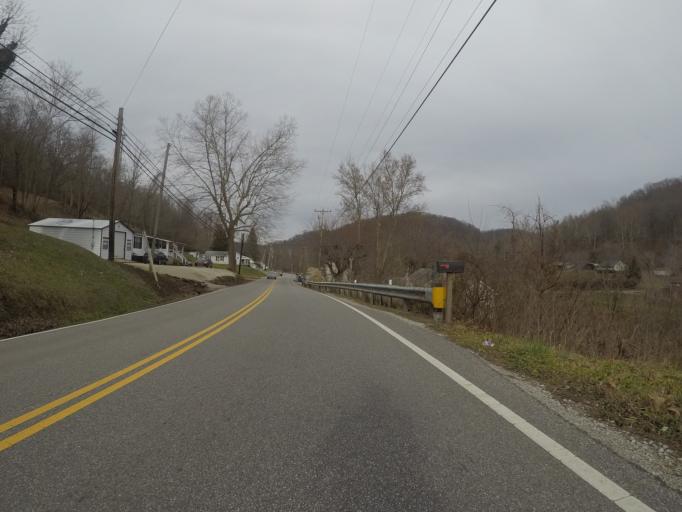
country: US
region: West Virginia
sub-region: Cabell County
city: Huntington
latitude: 38.4384
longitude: -82.4652
